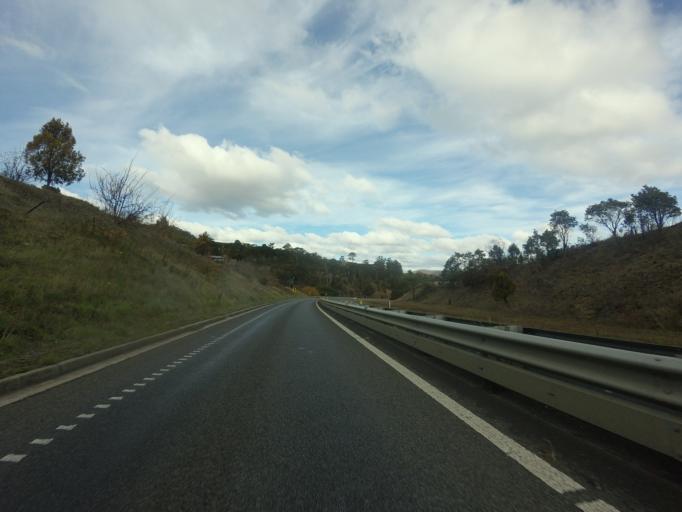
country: AU
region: Tasmania
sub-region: Brighton
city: Bridgewater
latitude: -42.5772
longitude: 147.2261
